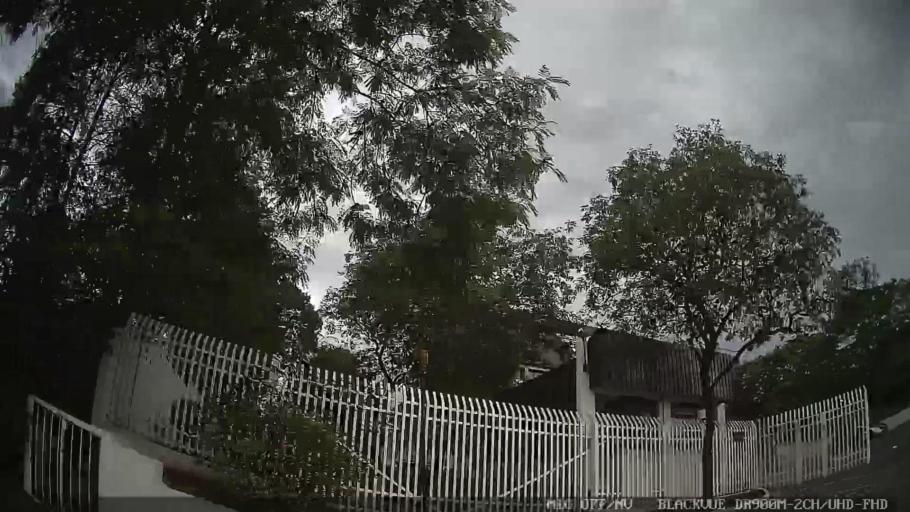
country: BR
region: Sao Paulo
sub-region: Jaguariuna
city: Jaguariuna
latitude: -22.6908
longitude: -46.9803
